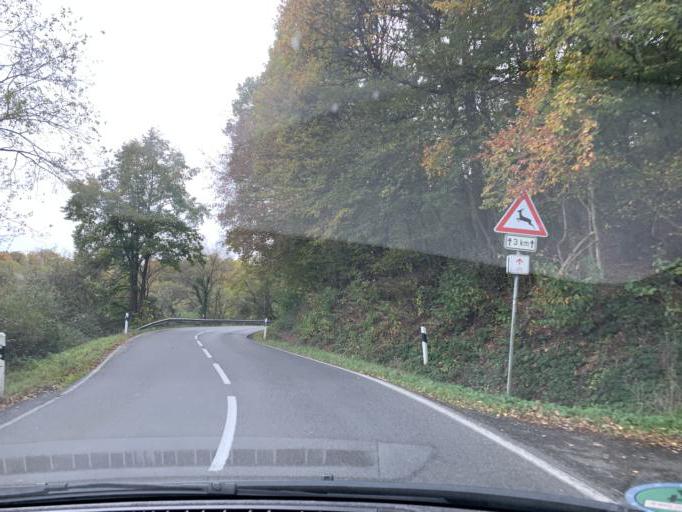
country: DE
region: North Rhine-Westphalia
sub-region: Regierungsbezirk Koln
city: Nideggen
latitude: 50.6851
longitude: 6.4579
